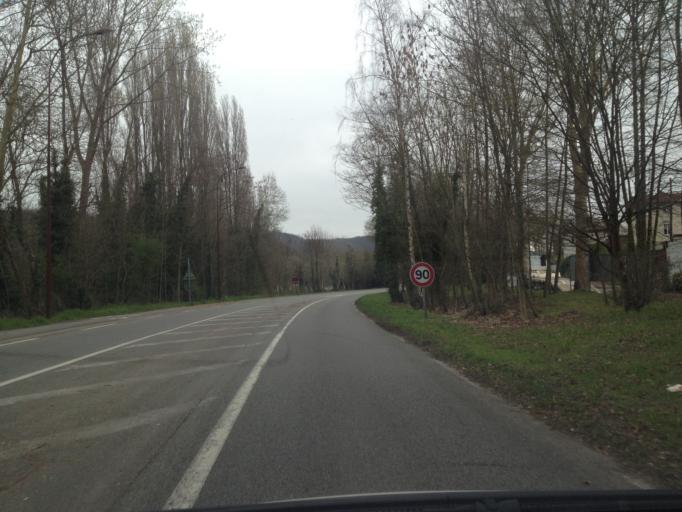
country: FR
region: Ile-de-France
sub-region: Departement des Yvelines
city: Jouy-en-Josas
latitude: 48.7616
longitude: 2.1797
